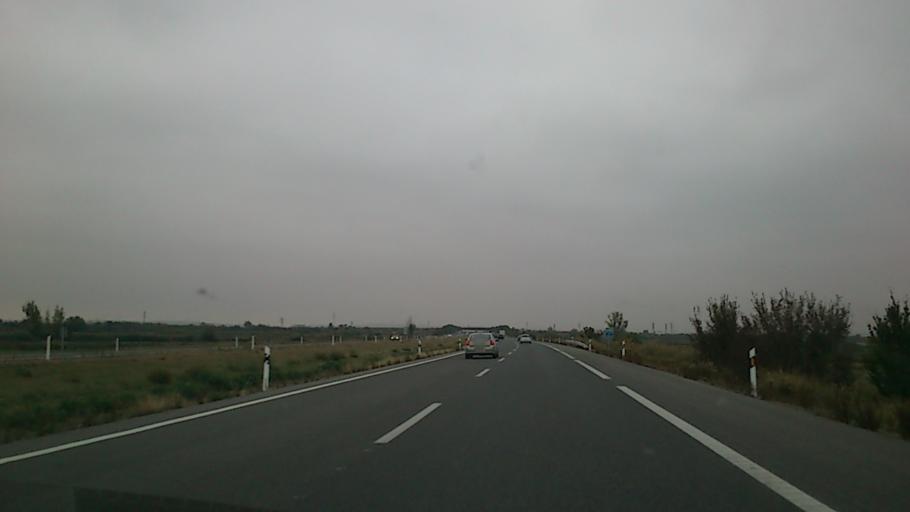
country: ES
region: Aragon
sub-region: Provincia de Zaragoza
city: Figueruelas
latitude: 41.7727
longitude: -1.1841
